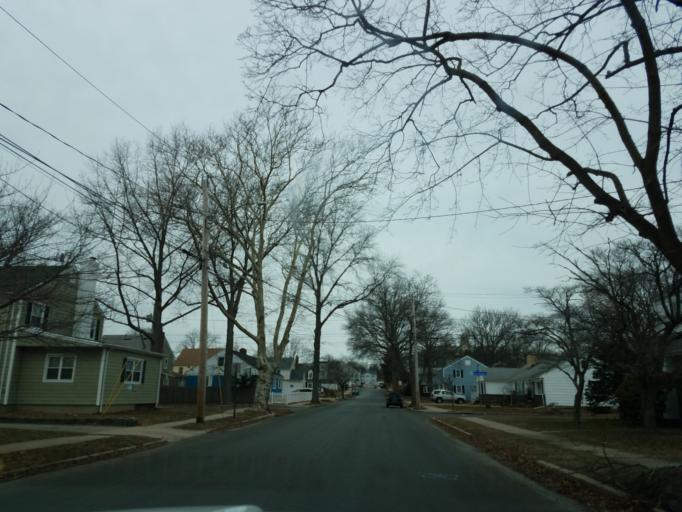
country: US
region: Connecticut
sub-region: Fairfield County
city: Bridgeport
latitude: 41.1881
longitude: -73.2139
